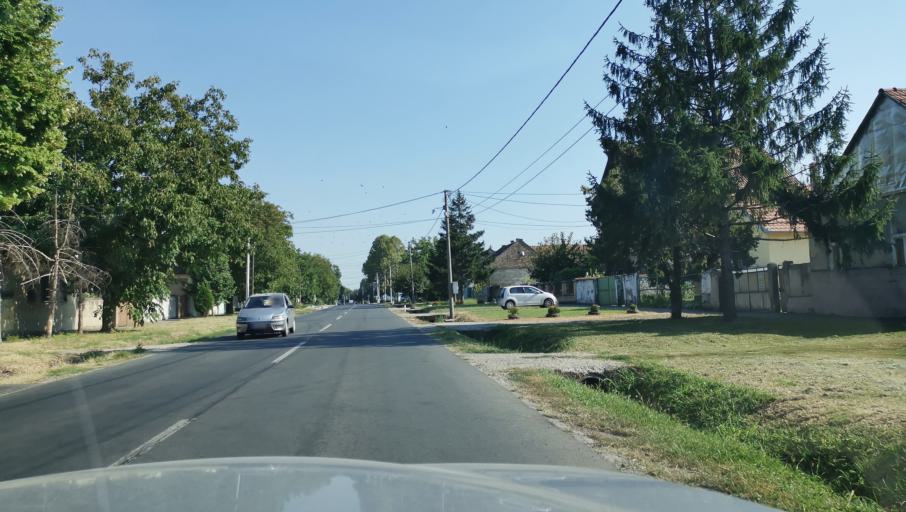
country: RS
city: Dobanovci
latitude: 44.8369
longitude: 20.2159
